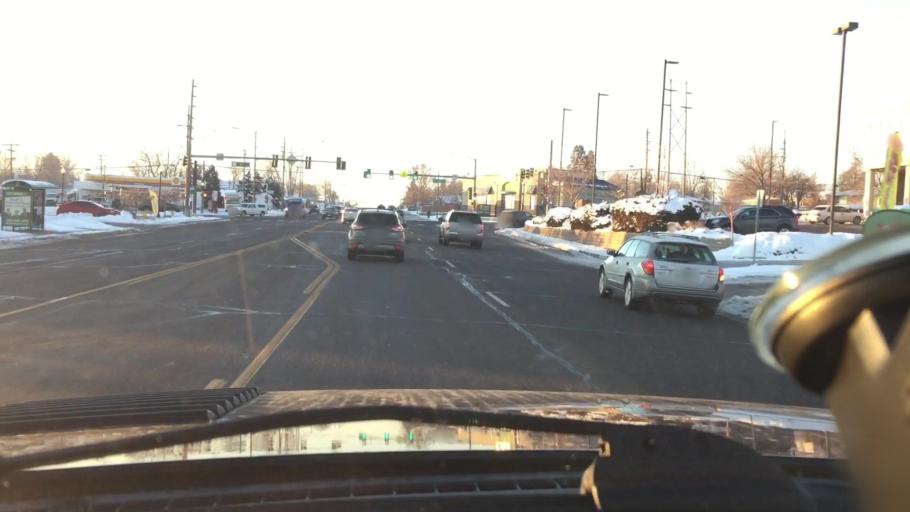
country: US
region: Colorado
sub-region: Adams County
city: Federal Heights
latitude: 39.8499
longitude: -105.0061
